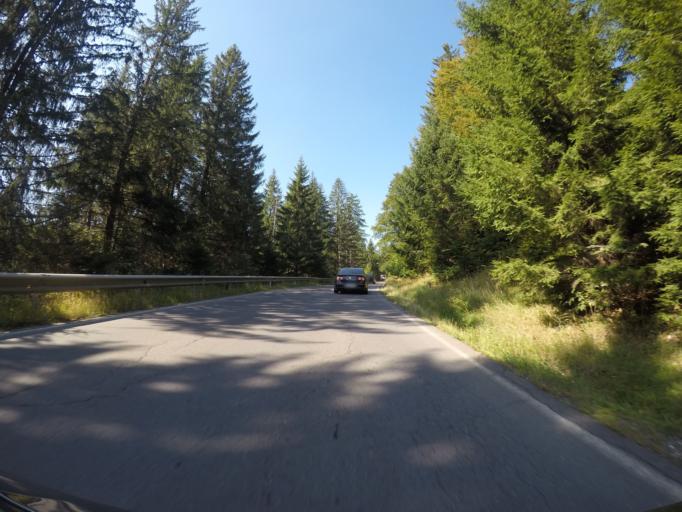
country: RO
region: Brasov
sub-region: Comuna Cristian
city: Cristian
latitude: 45.5886
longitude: 25.5215
